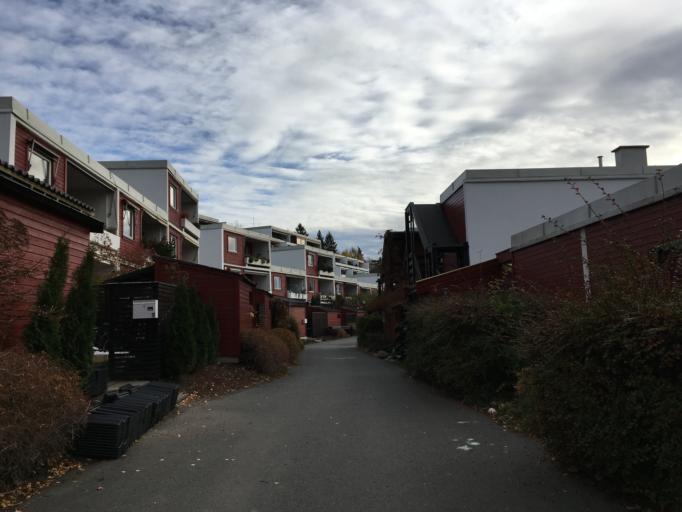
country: NO
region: Akershus
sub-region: Baerum
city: Lysaker
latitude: 59.9351
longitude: 10.6369
